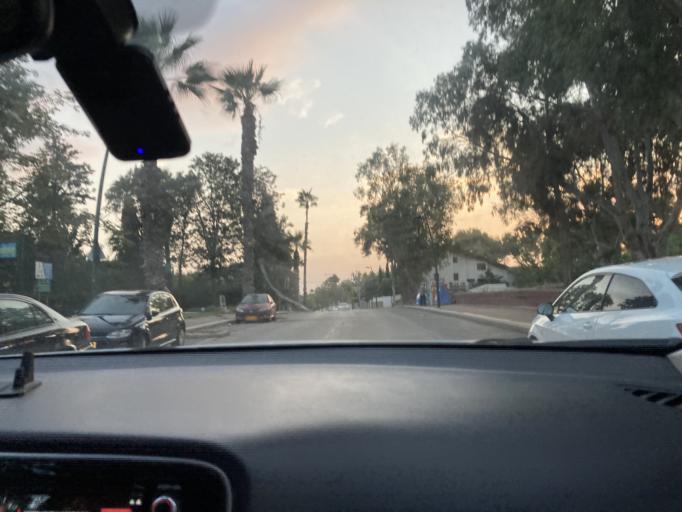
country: IL
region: Tel Aviv
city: Ramat HaSharon
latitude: 32.1507
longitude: 34.8288
